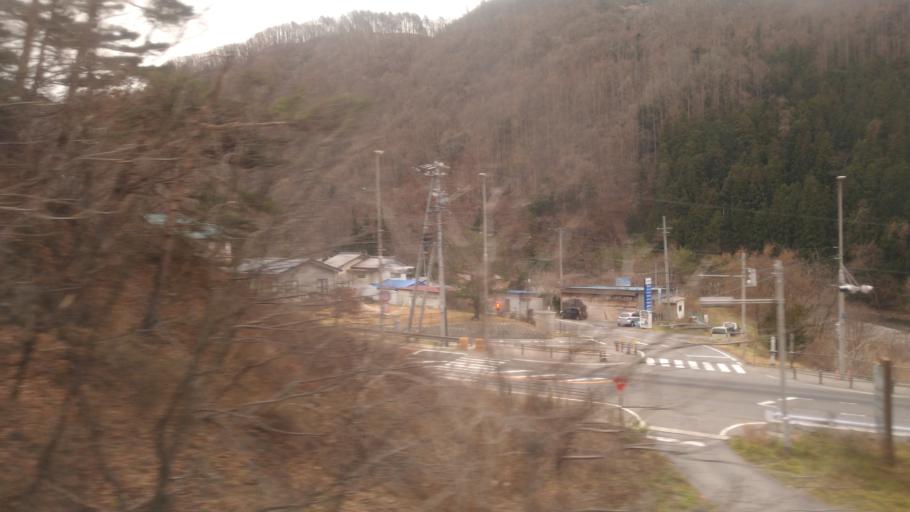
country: JP
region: Nagano
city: Tatsuno
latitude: 35.9985
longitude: 137.8513
